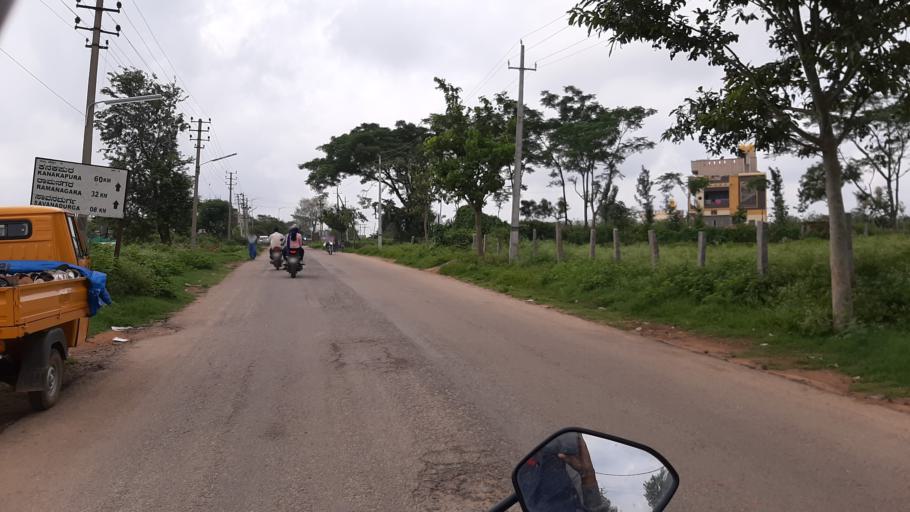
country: IN
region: Karnataka
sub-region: Ramanagara
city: Magadi
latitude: 12.9502
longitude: 77.2377
